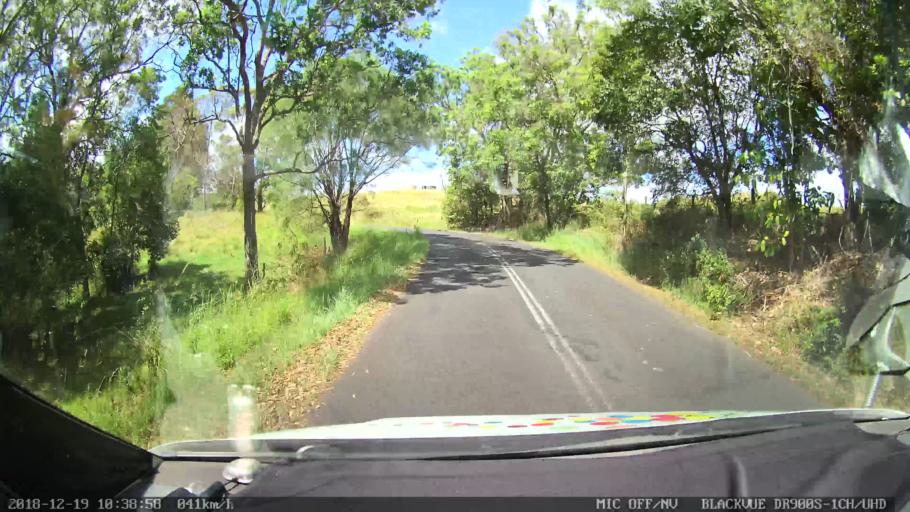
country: AU
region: New South Wales
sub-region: Lismore Municipality
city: Nimbin
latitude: -28.5778
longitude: 153.1546
